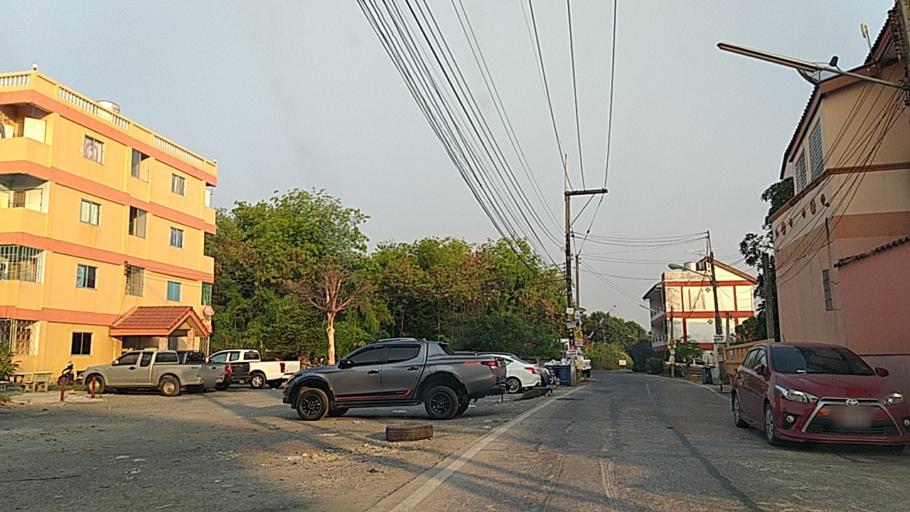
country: TH
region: Phra Nakhon Si Ayutthaya
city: Ban Bang Kadi Pathum Thani
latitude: 13.9960
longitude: 100.5549
